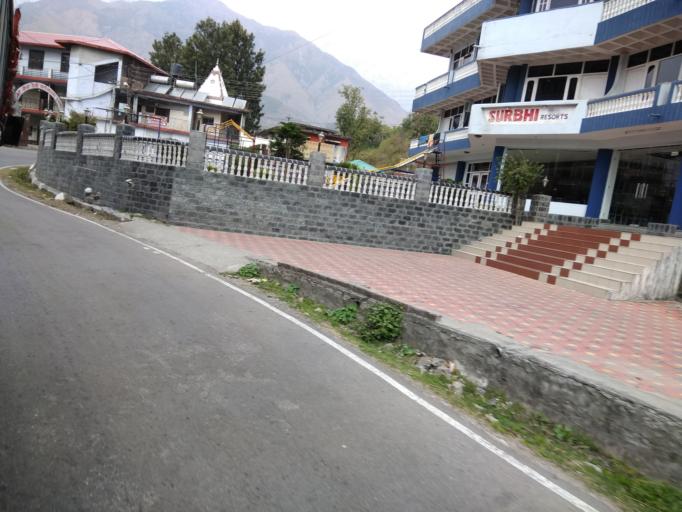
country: IN
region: Himachal Pradesh
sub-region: Kangra
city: Dharmsala
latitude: 32.1481
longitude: 76.4227
